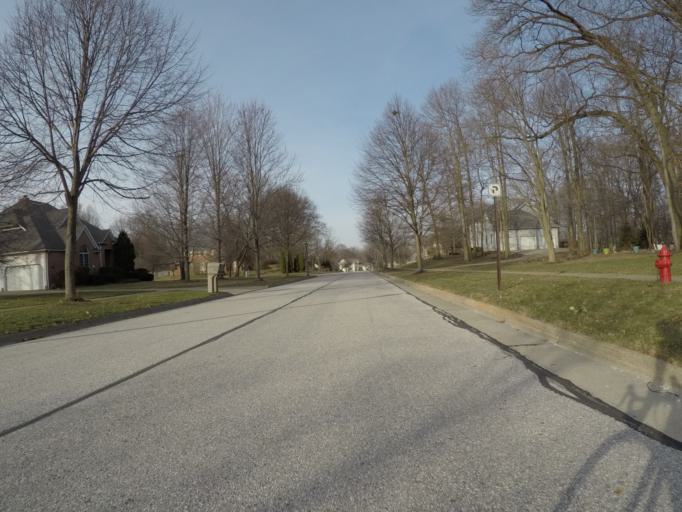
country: US
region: Ohio
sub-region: Portage County
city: Kent
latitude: 41.1584
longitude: -81.3424
